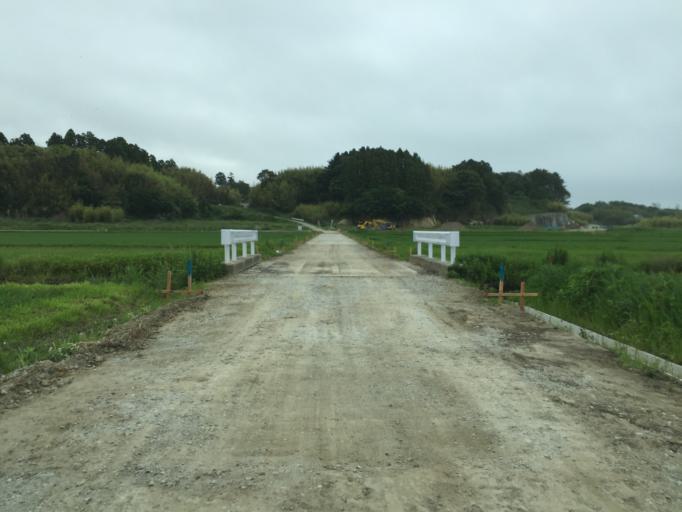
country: JP
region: Fukushima
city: Namie
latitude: 37.7577
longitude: 140.9967
